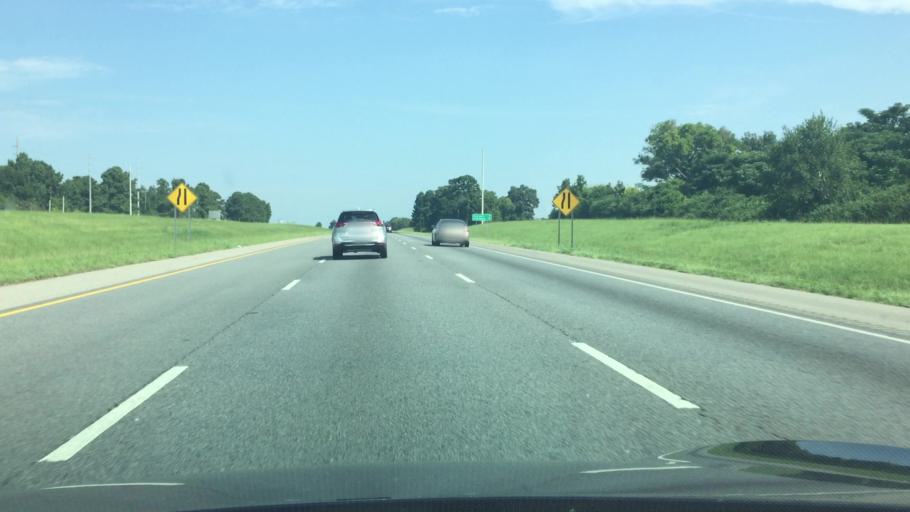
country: US
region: Alabama
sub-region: Autauga County
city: Prattville
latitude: 32.4989
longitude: -86.4161
